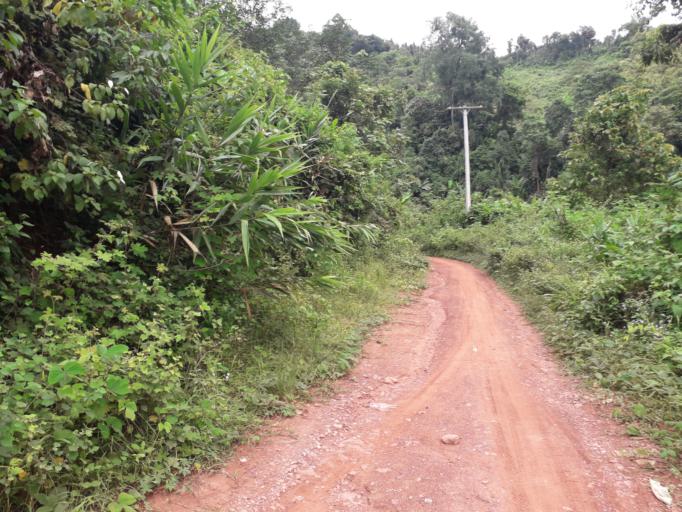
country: CN
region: Yunnan
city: Menglie
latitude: 22.1884
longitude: 101.7019
